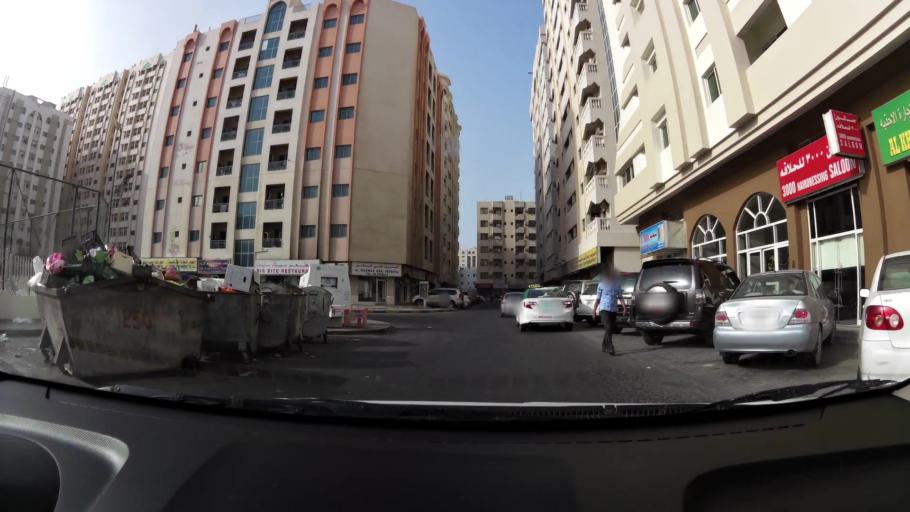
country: AE
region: Ash Shariqah
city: Sharjah
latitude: 25.3355
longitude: 55.3969
